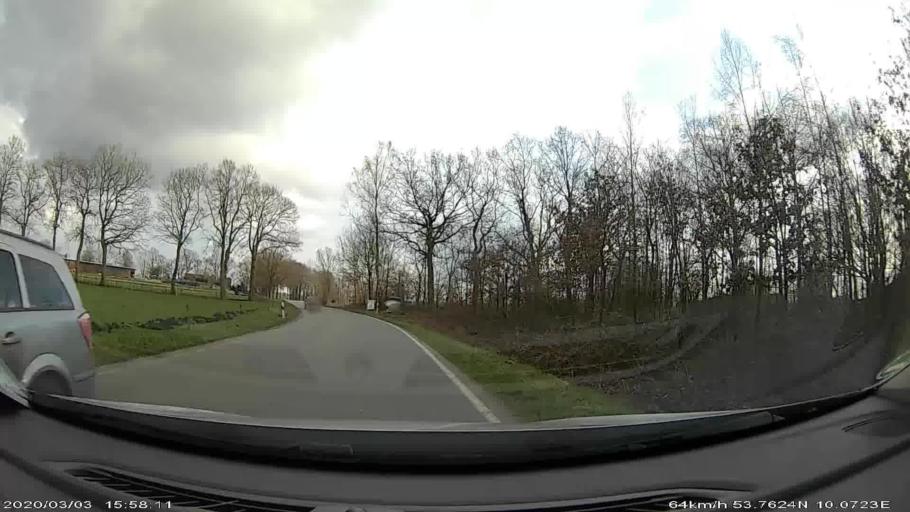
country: DE
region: Schleswig-Holstein
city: Tangstedt
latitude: 53.7637
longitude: 10.0721
